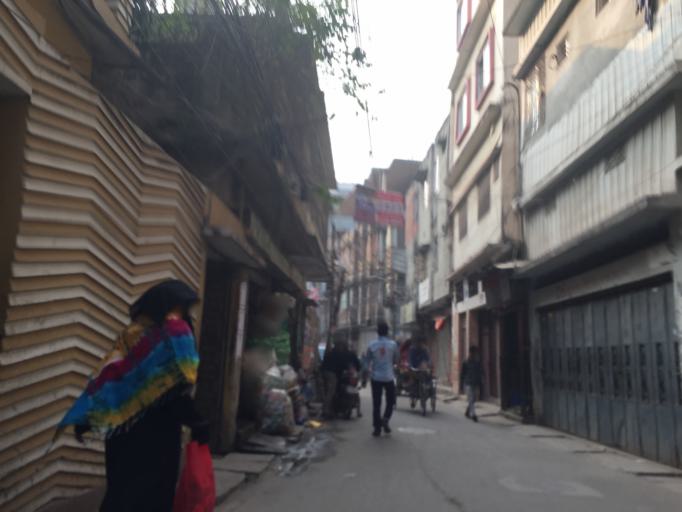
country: BD
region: Dhaka
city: Azimpur
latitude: 23.7218
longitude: 90.3810
